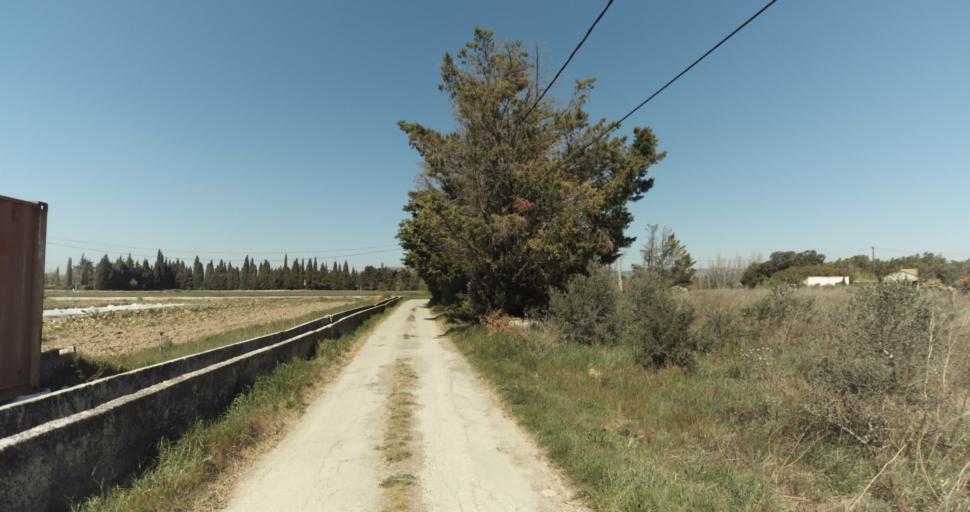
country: FR
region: Provence-Alpes-Cote d'Azur
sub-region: Departement des Bouches-du-Rhone
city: Pelissanne
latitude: 43.6182
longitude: 5.1510
